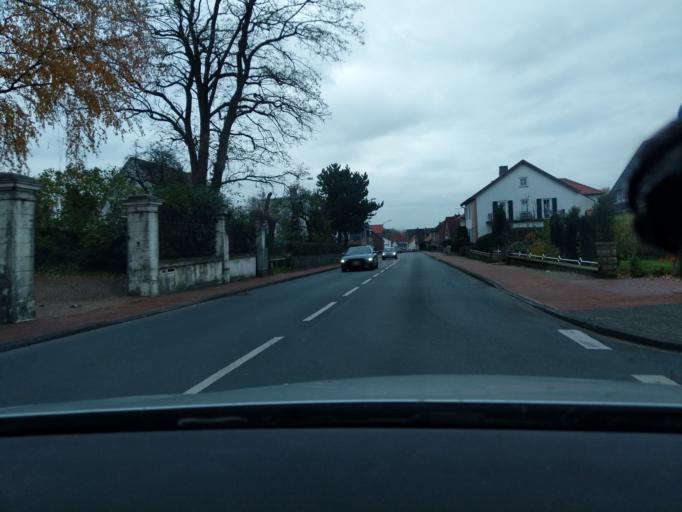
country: DE
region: North Rhine-Westphalia
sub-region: Regierungsbezirk Munster
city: Birgte
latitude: 52.2623
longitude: 7.6225
